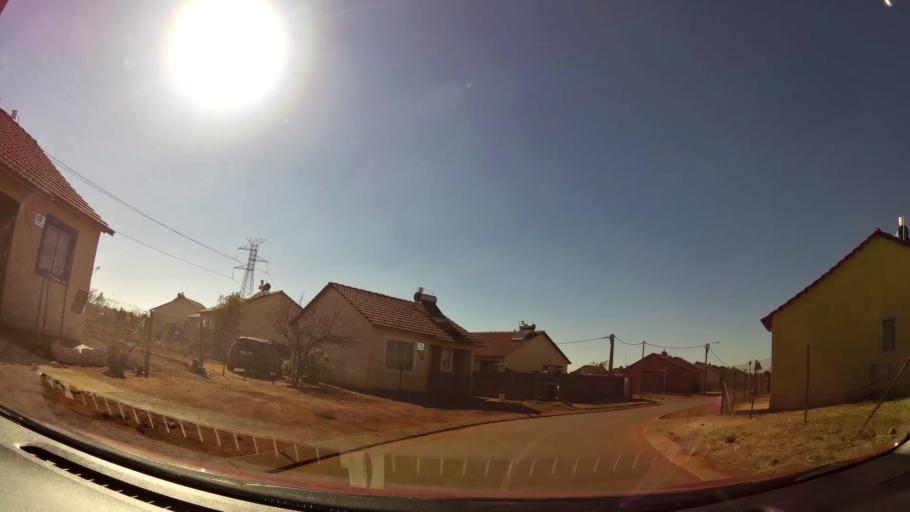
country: ZA
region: Gauteng
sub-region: City of Johannesburg Metropolitan Municipality
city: Soweto
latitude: -26.2328
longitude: 27.8008
